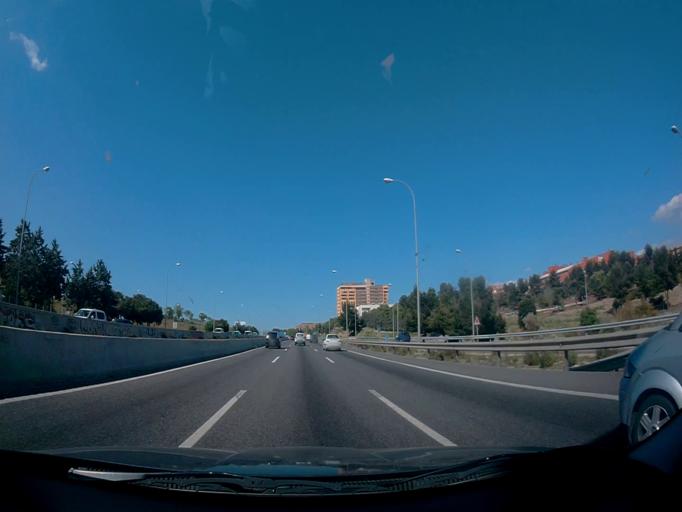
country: ES
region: Madrid
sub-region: Provincia de Madrid
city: Vicalvaro
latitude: 40.3941
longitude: -3.6288
